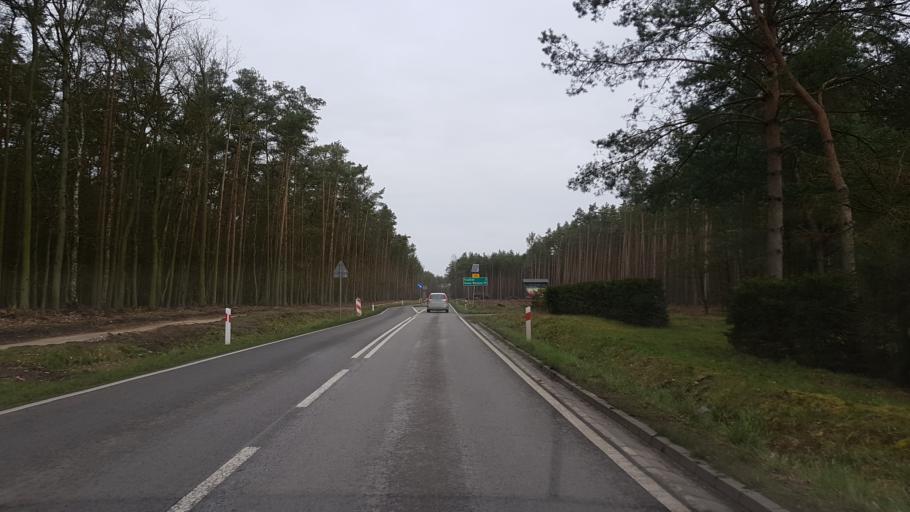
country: PL
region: West Pomeranian Voivodeship
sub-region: Powiat policki
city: Police
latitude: 53.6291
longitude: 14.5023
